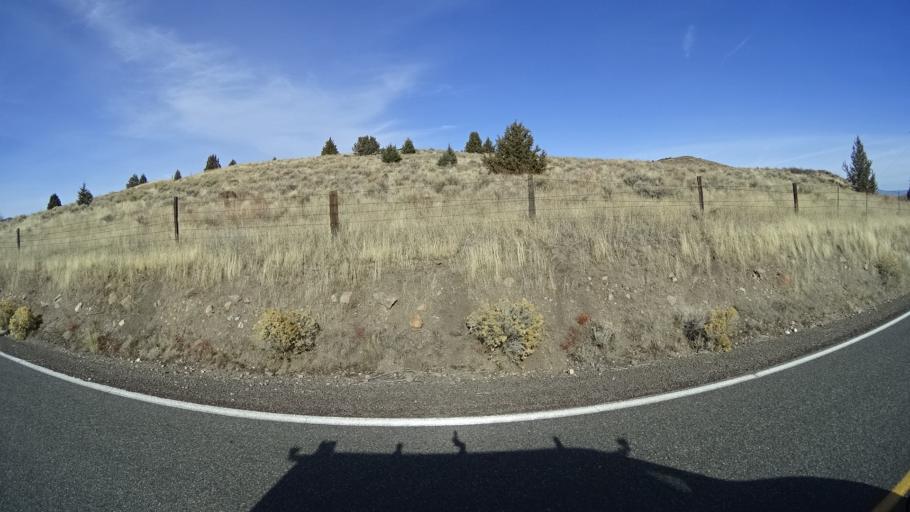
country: US
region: California
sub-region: Siskiyou County
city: Weed
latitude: 41.5374
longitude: -122.5050
